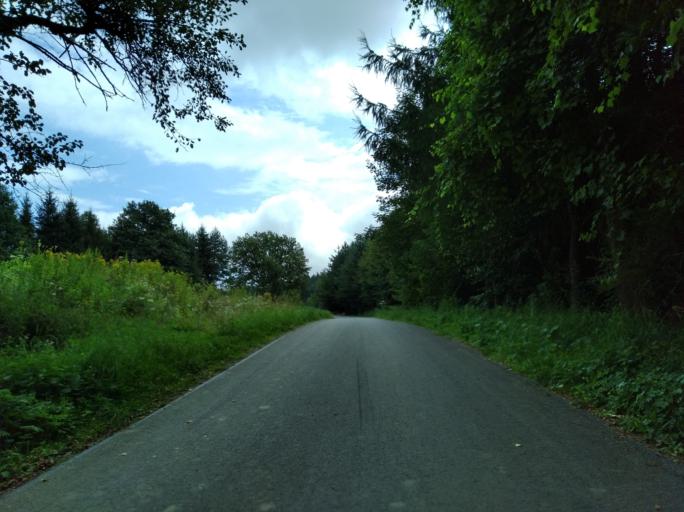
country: PL
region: Subcarpathian Voivodeship
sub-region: Powiat krosnienski
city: Wojaszowka
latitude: 49.7816
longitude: 21.7066
